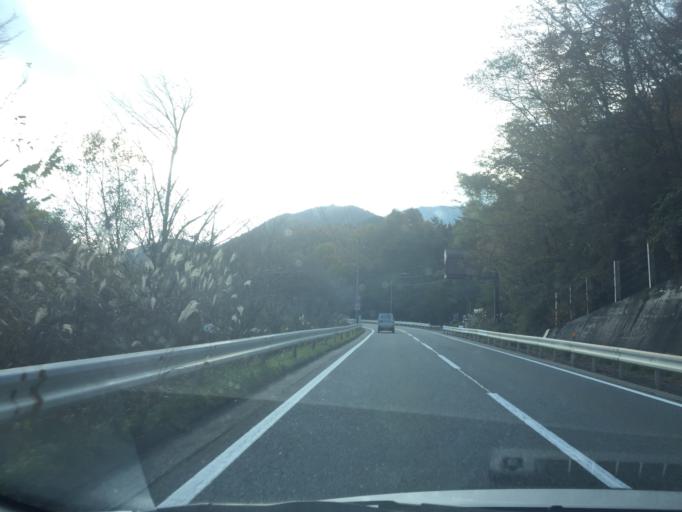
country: JP
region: Gifu
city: Nakatsugawa
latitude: 35.3688
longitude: 137.6747
